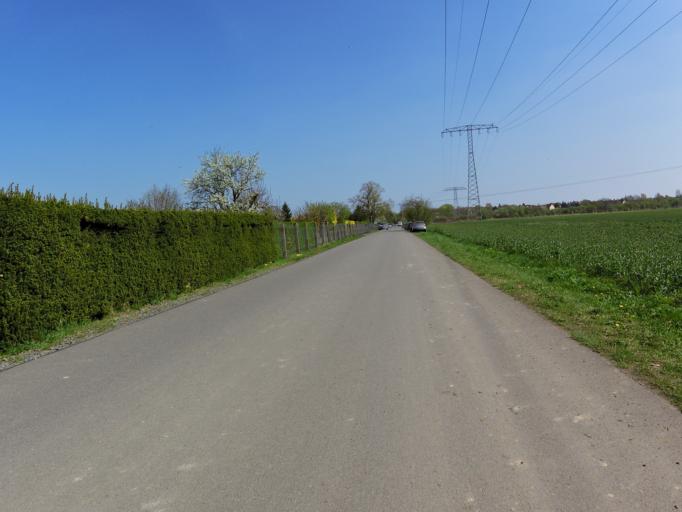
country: DE
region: Saxony
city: Leipzig
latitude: 51.3912
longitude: 12.3100
